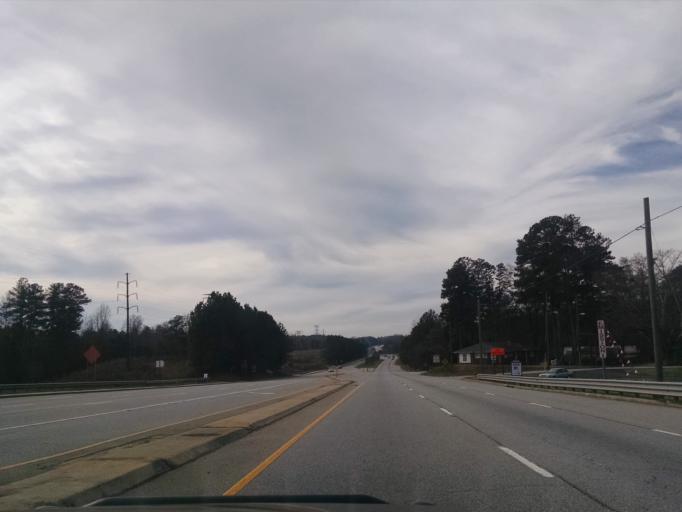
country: US
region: Georgia
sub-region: Gwinnett County
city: Sugar Hill
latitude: 34.1043
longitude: -84.0315
